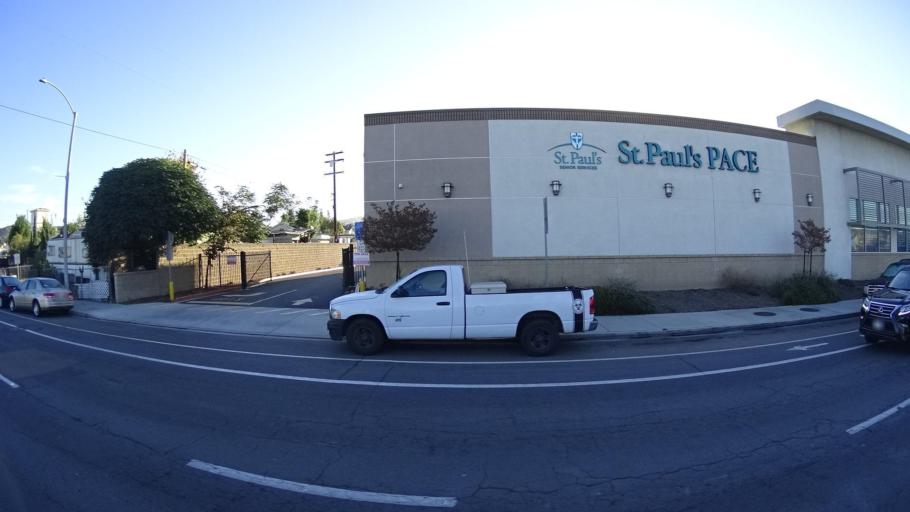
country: US
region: California
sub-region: San Diego County
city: Bostonia
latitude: 32.8085
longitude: -116.9358
